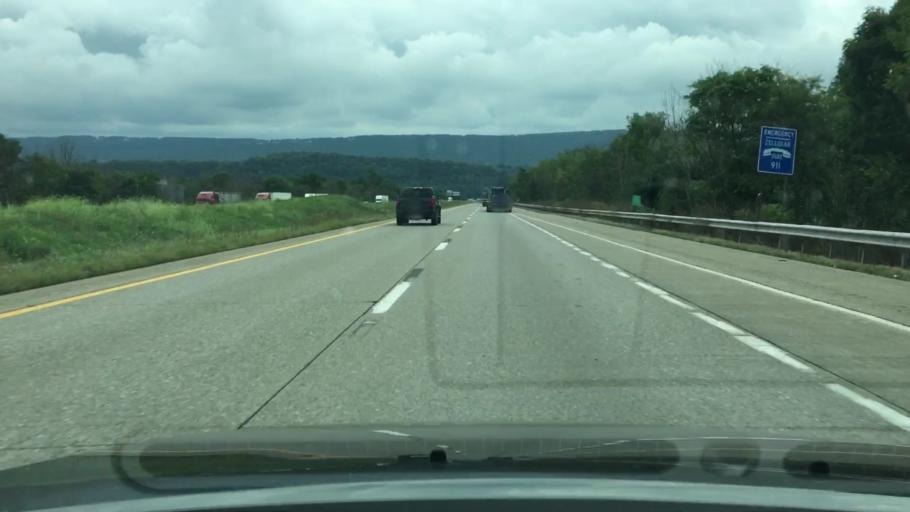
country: US
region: Pennsylvania
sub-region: Luzerne County
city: Conyngham
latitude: 41.0371
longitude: -76.0141
